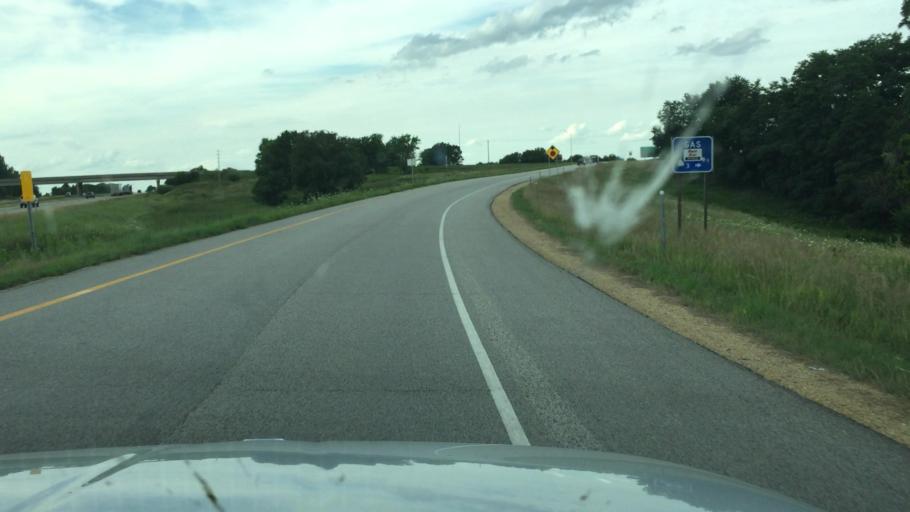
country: US
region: Iowa
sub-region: Scott County
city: Buffalo
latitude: 41.5351
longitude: -90.6755
